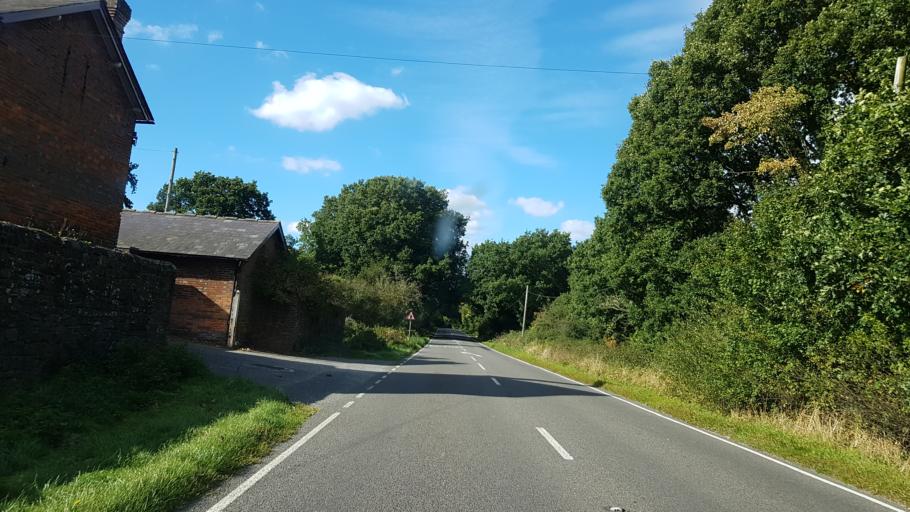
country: GB
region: England
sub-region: West Sussex
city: Petworth
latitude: 50.9970
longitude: -0.6146
